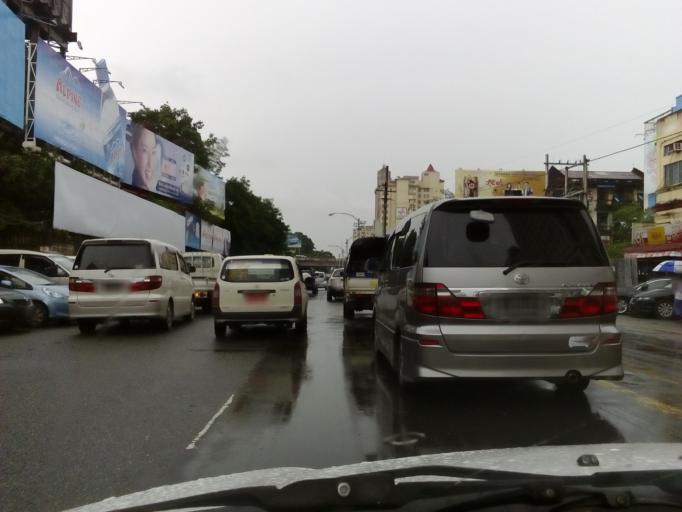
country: MM
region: Yangon
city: Yangon
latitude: 16.7794
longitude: 96.1597
